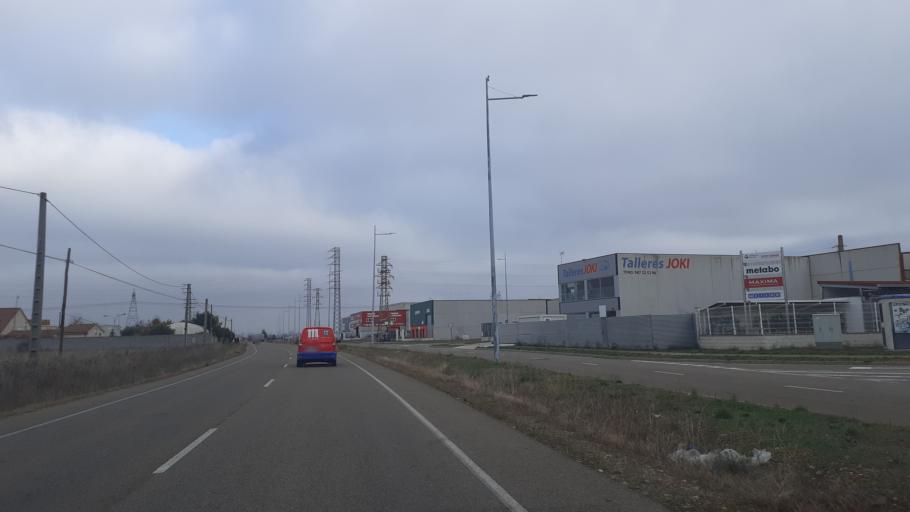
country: ES
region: Castille and Leon
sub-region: Provincia de Leon
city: Onzonilla
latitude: 42.5501
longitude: -5.5856
